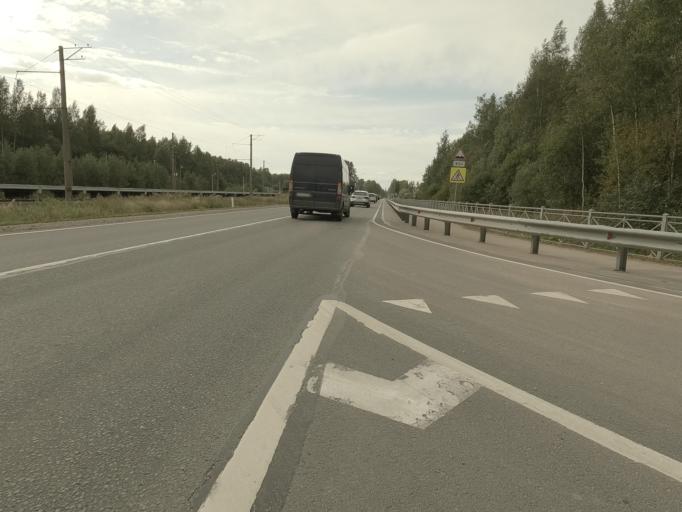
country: RU
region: Leningrad
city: Kirovsk
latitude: 59.8542
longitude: 31.0179
